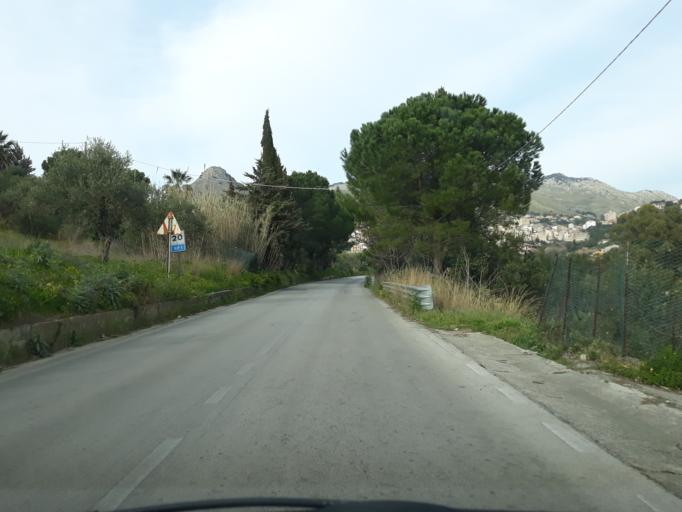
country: IT
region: Sicily
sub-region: Palermo
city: Giardinello
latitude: 38.0796
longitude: 13.1619
